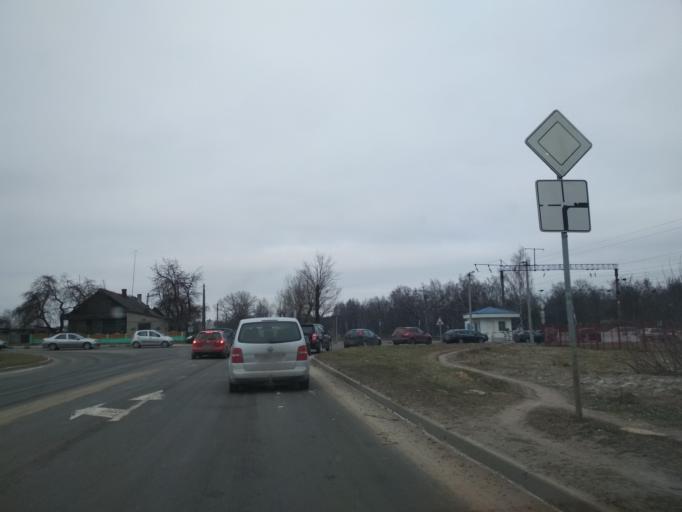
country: BY
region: Minsk
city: Mar''ina Horka
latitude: 53.5167
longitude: 28.1387
